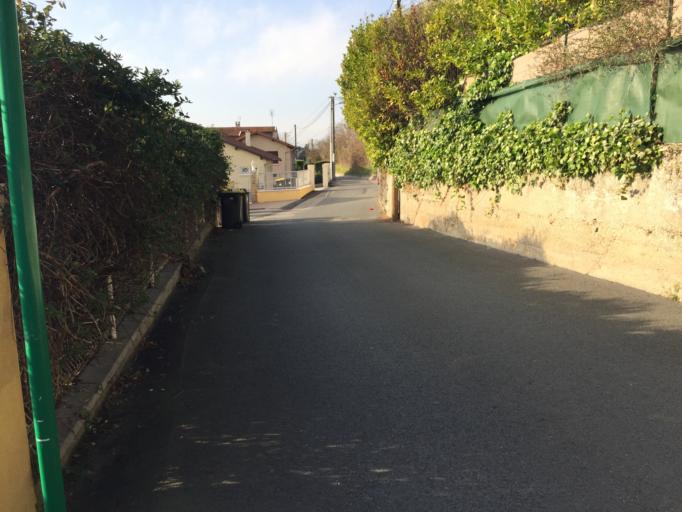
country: FR
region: Rhone-Alpes
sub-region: Departement de l'Ain
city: Saint-Maurice-de-Beynost
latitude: 45.8344
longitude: 4.9905
